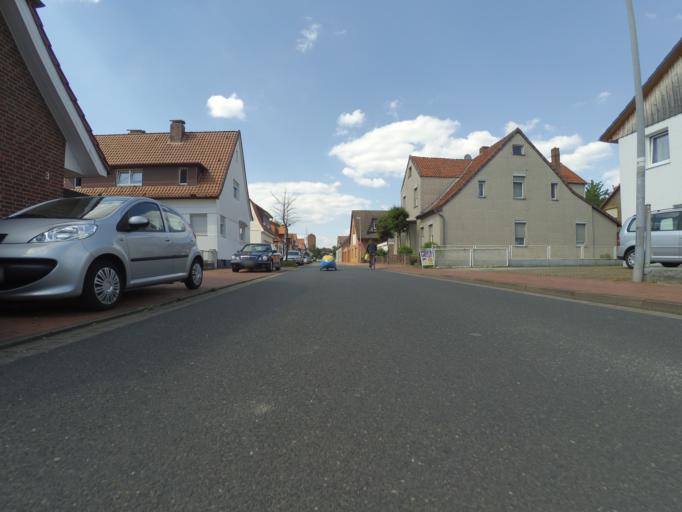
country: DE
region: Lower Saxony
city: Burgdorf
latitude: 52.4488
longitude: 10.0101
